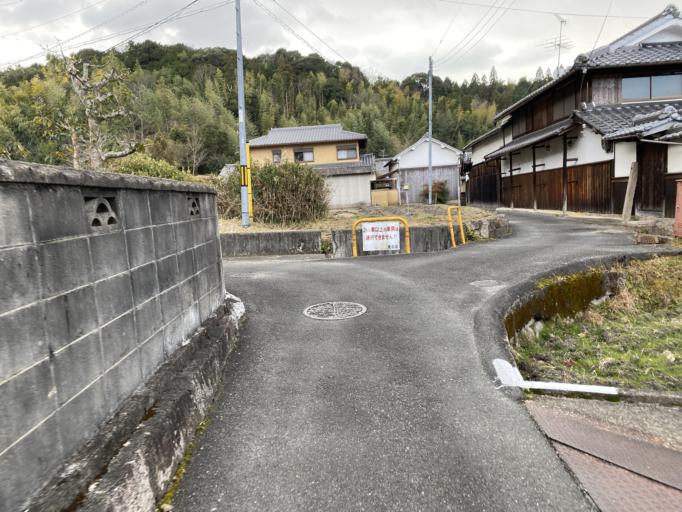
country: JP
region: Nara
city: Nara-shi
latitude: 34.7540
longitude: 135.8762
